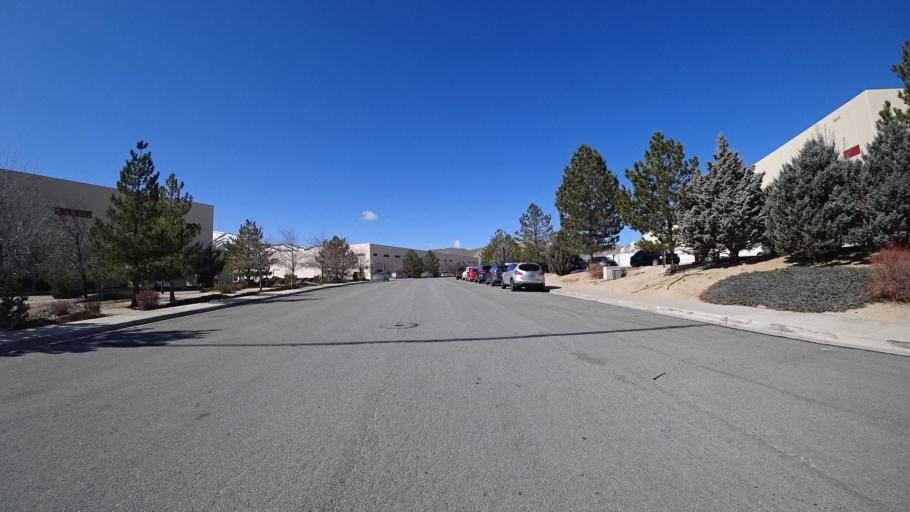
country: US
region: Nevada
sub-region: Washoe County
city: Lemmon Valley
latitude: 39.6547
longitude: -119.8999
